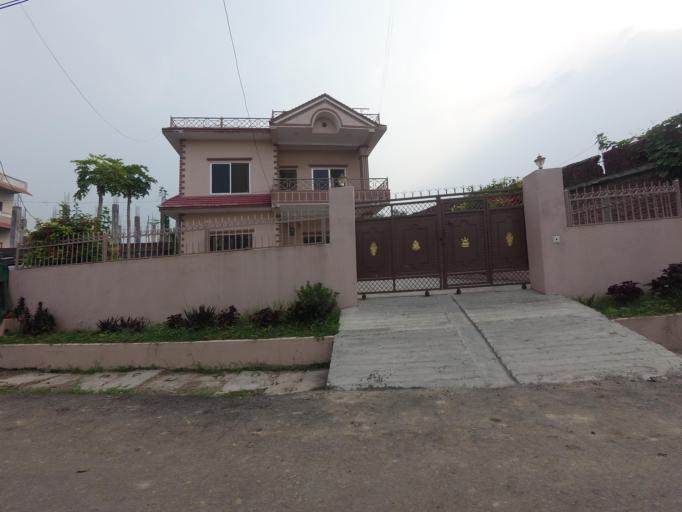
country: NP
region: Western Region
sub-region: Lumbini Zone
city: Bhairahawa
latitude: 27.5243
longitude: 83.4533
